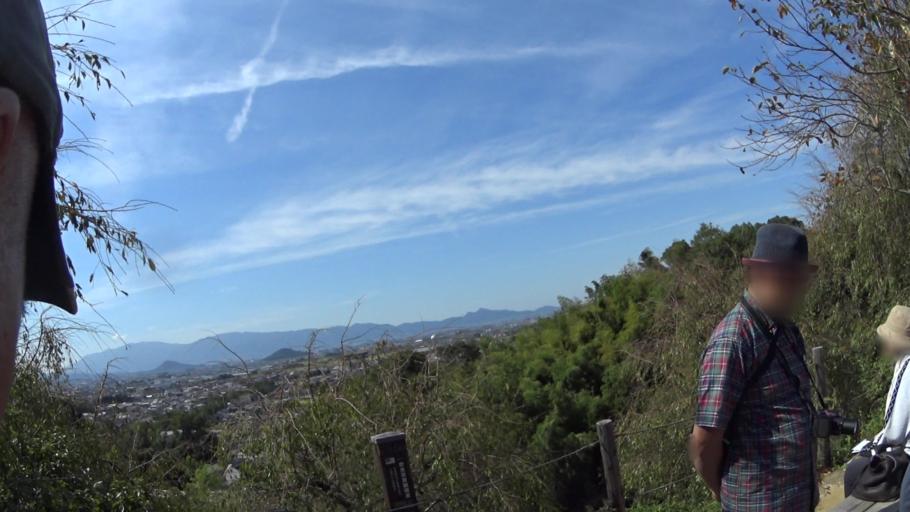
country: JP
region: Nara
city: Sakurai
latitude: 34.5310
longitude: 135.8520
